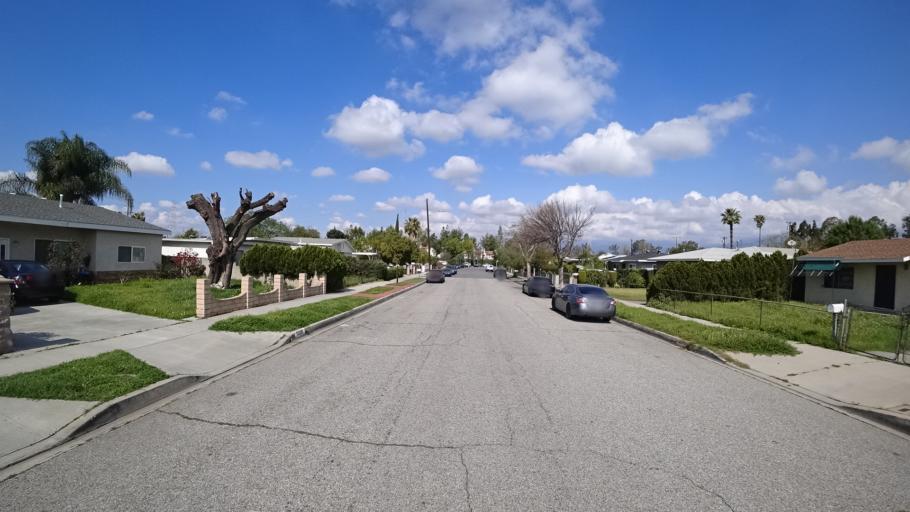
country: US
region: California
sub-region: Los Angeles County
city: Baldwin Park
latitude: 34.0785
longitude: -117.9854
